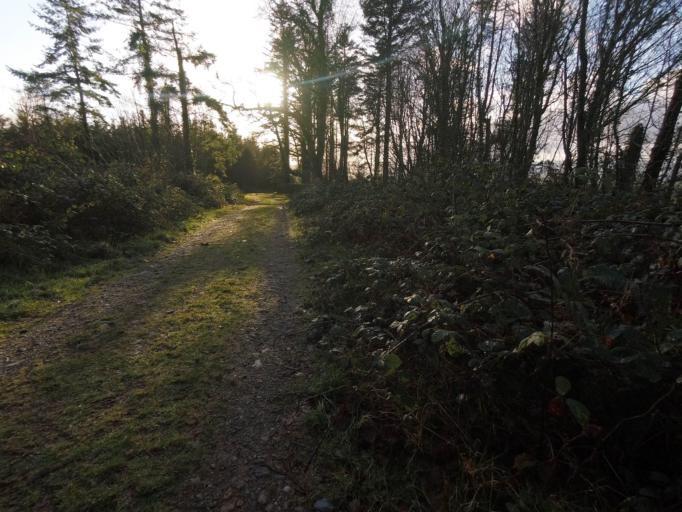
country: IE
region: Munster
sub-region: Waterford
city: Portlaw
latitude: 52.3089
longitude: -7.3565
